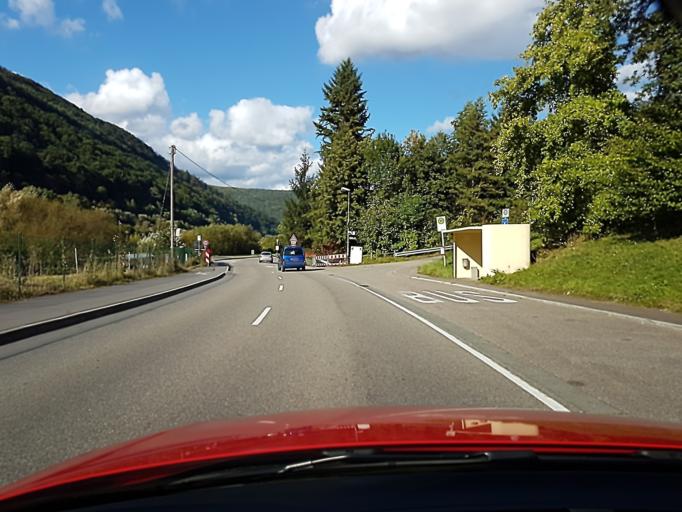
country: DE
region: Hesse
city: Neckarsteinach
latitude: 49.3950
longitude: 8.8233
